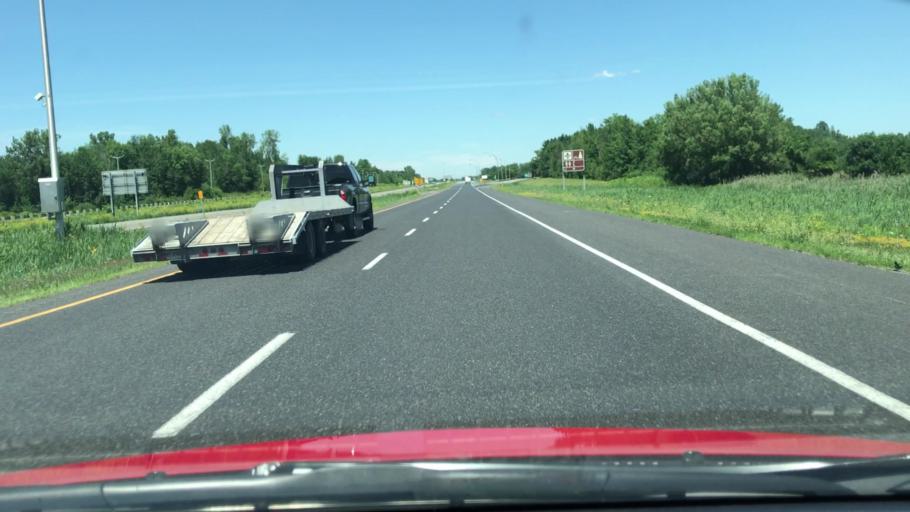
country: US
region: New York
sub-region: Clinton County
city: Champlain
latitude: 45.0419
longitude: -73.4535
